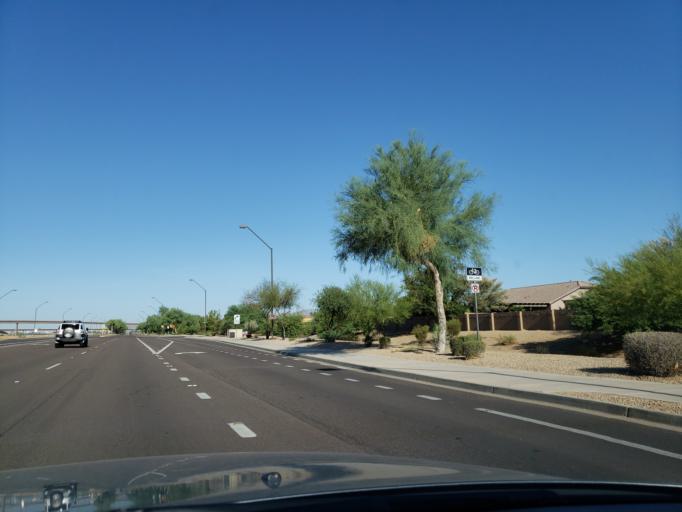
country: US
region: Arizona
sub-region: Maricopa County
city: Litchfield Park
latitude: 33.4647
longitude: -112.4164
